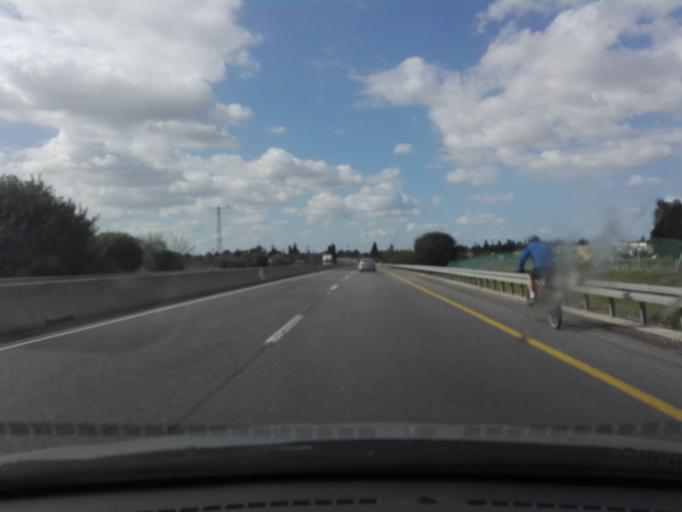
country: PS
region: West Bank
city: Nazlat `Isa
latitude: 32.4697
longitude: 35.0067
